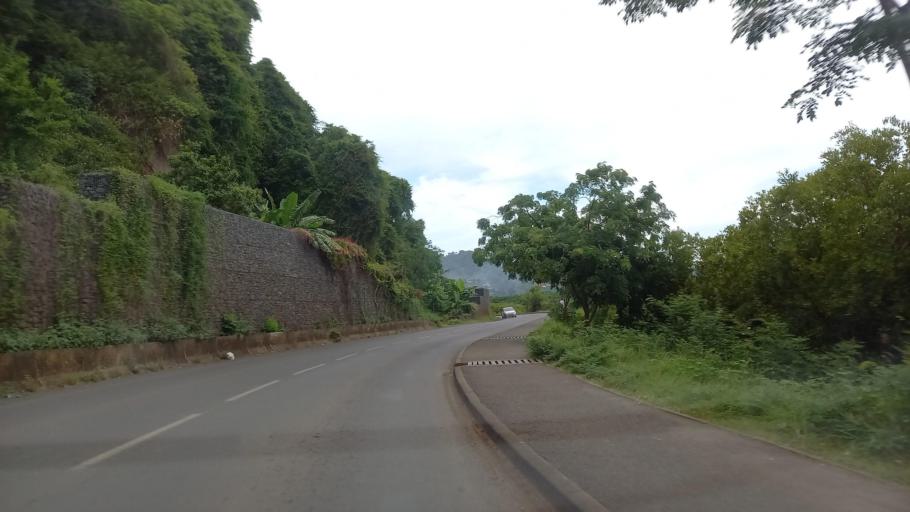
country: YT
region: Mamoudzou
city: Mamoudzou
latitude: -12.7755
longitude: 45.2307
